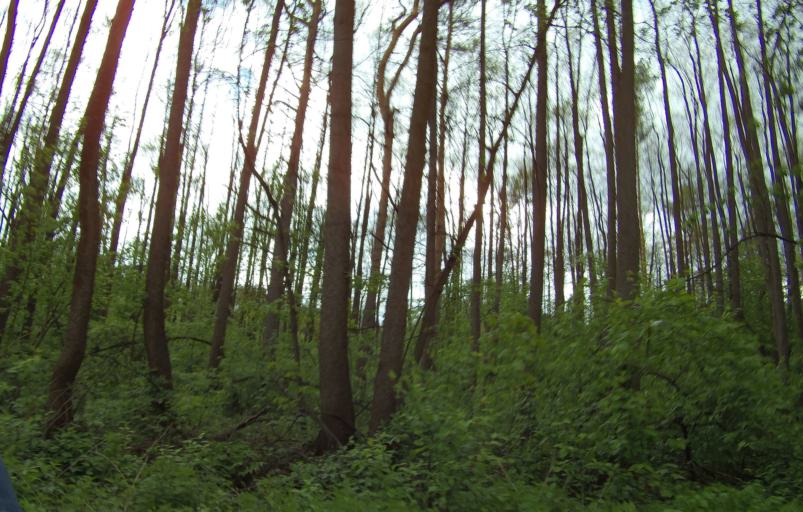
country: RU
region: Moskovskaya
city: Kratovo
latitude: 55.5840
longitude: 38.1696
